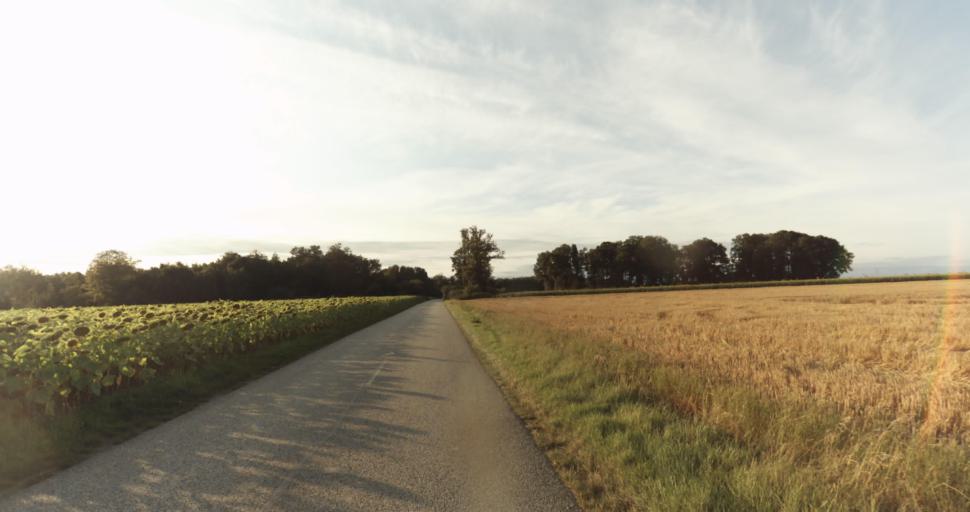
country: FR
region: Haute-Normandie
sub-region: Departement de l'Eure
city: Saint-Germain-sur-Avre
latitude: 48.8291
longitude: 1.2605
